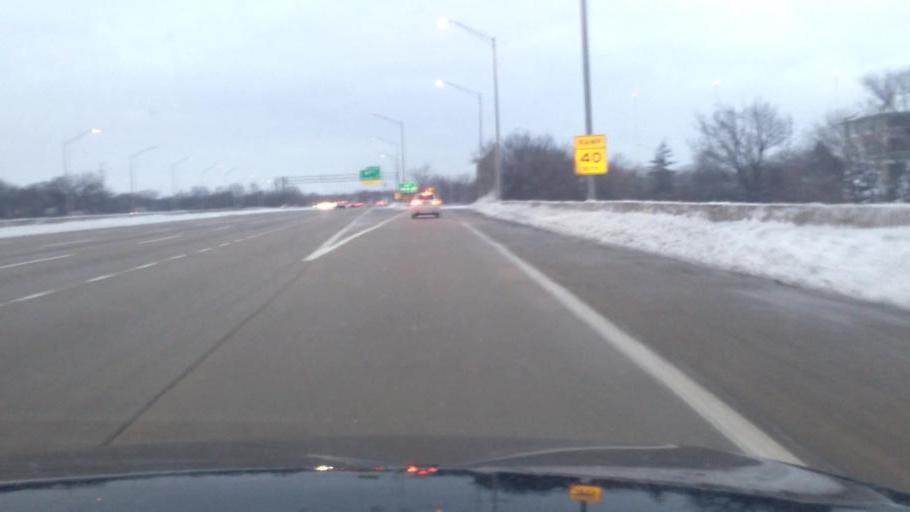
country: US
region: Illinois
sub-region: Cook County
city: Des Plaines
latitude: 42.0363
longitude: -87.8673
